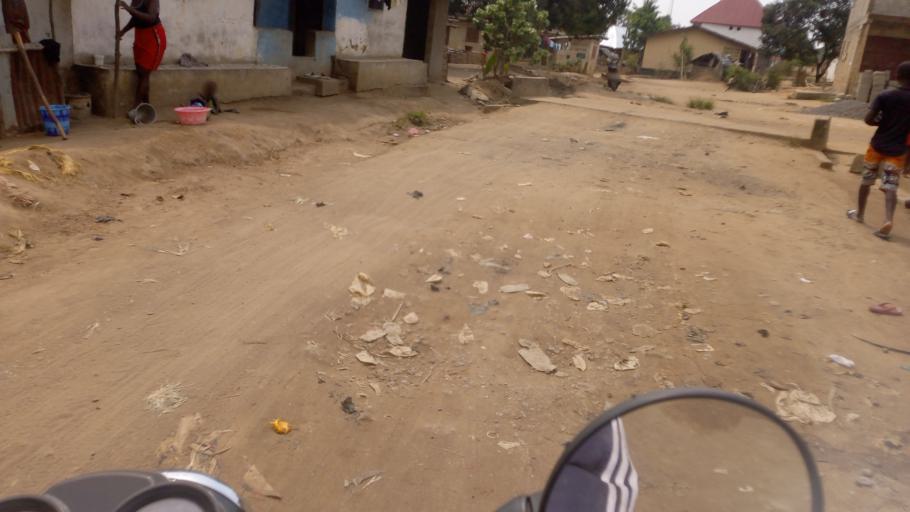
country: SL
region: Western Area
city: Waterloo
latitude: 8.3251
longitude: -13.0571
